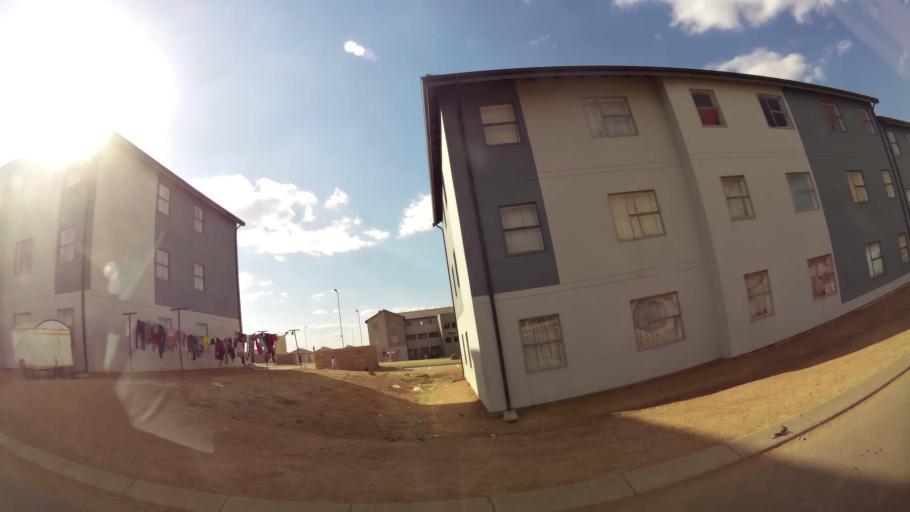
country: ZA
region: Gauteng
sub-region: Ekurhuleni Metropolitan Municipality
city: Tembisa
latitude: -25.9807
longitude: 28.1863
